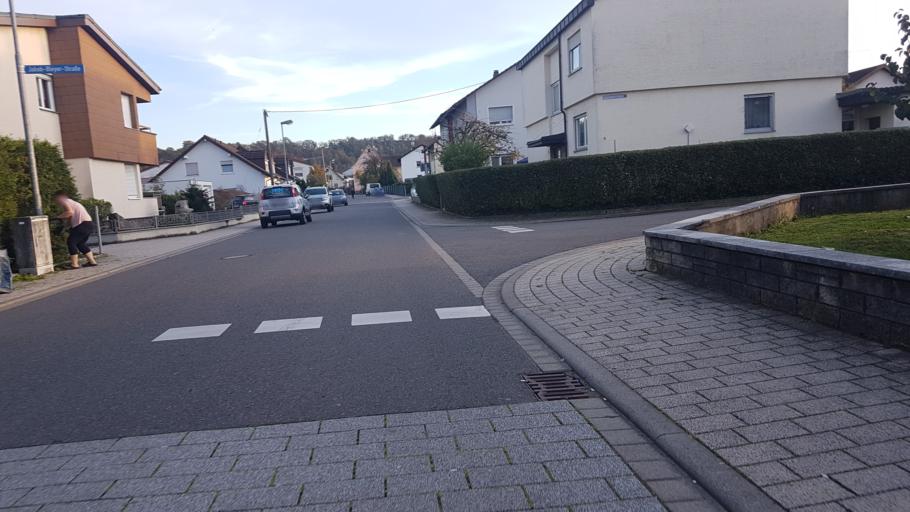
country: DE
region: Baden-Wuerttemberg
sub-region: Karlsruhe Region
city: Hassmersheim
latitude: 49.3042
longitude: 9.1463
